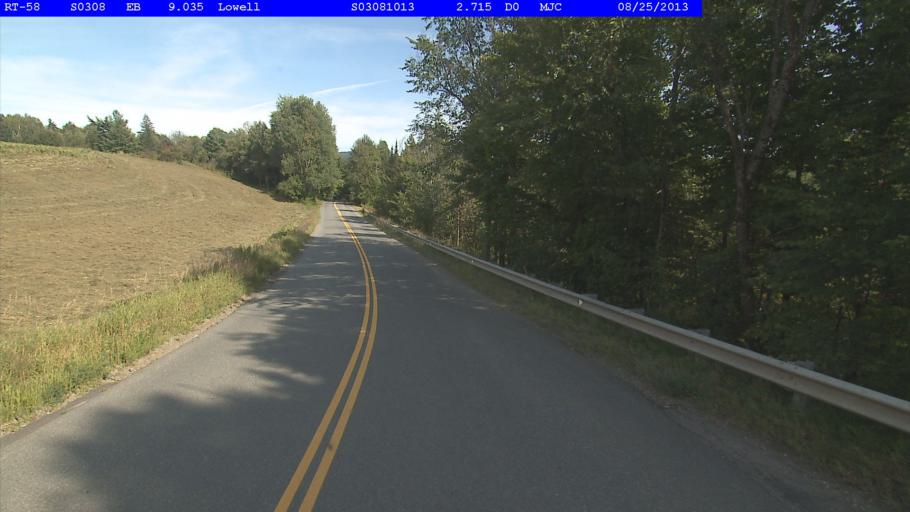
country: US
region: Vermont
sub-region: Lamoille County
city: Hyde Park
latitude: 44.8122
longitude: -72.4660
